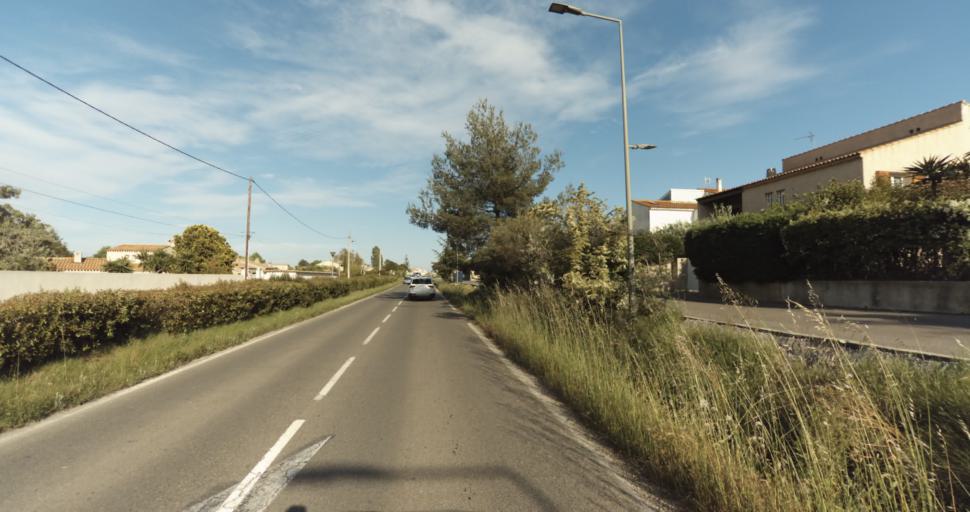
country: FR
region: Provence-Alpes-Cote d'Azur
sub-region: Departement du Var
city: Carqueiranne
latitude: 43.1187
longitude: 6.0751
